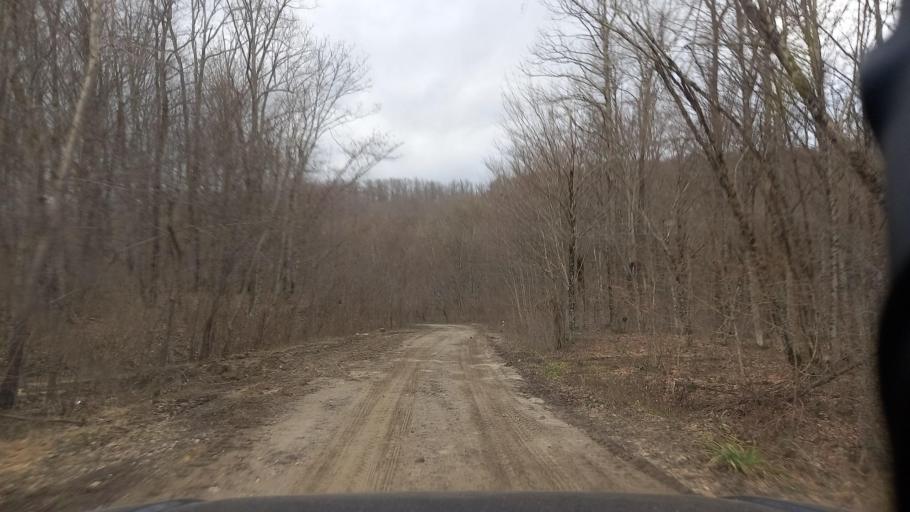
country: RU
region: Krasnodarskiy
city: Dzhubga
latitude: 44.4864
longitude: 38.7739
